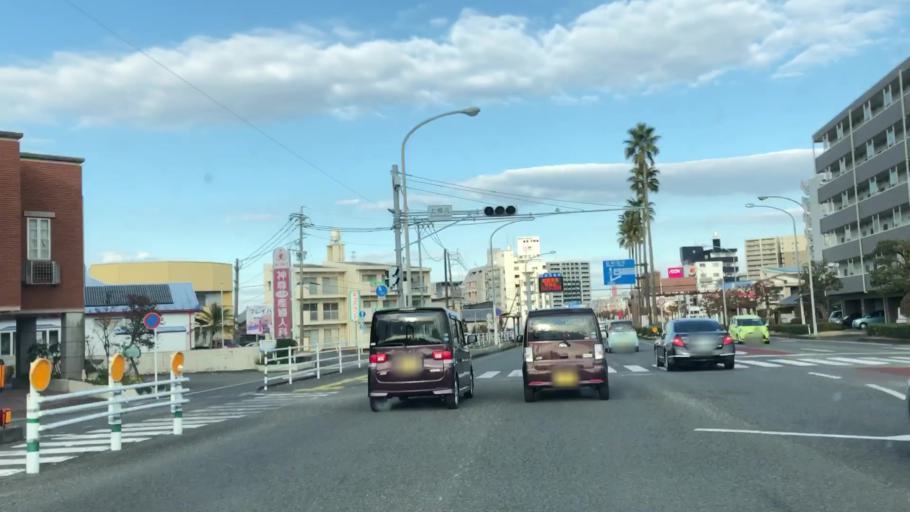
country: JP
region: Miyazaki
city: Miyazaki-shi
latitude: 31.8905
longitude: 131.4135
